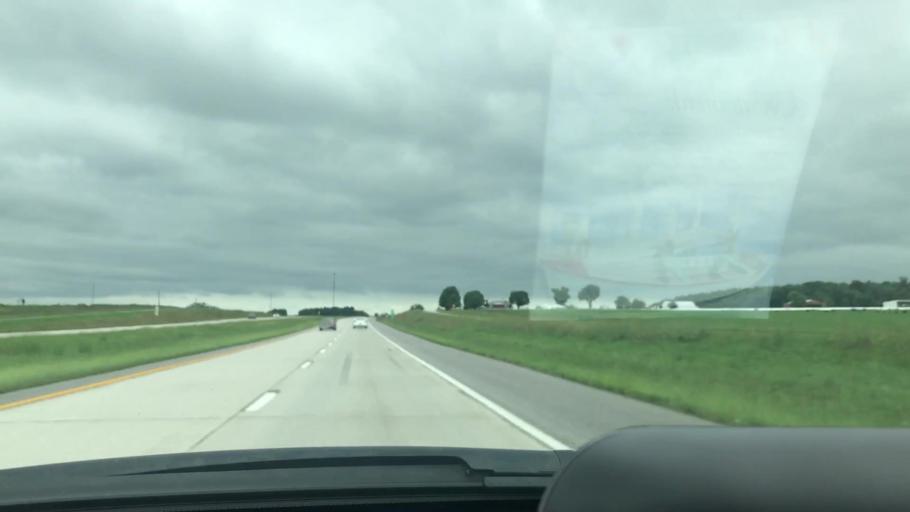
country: US
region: Missouri
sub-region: Greene County
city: Fair Grove
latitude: 37.4416
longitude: -93.1443
